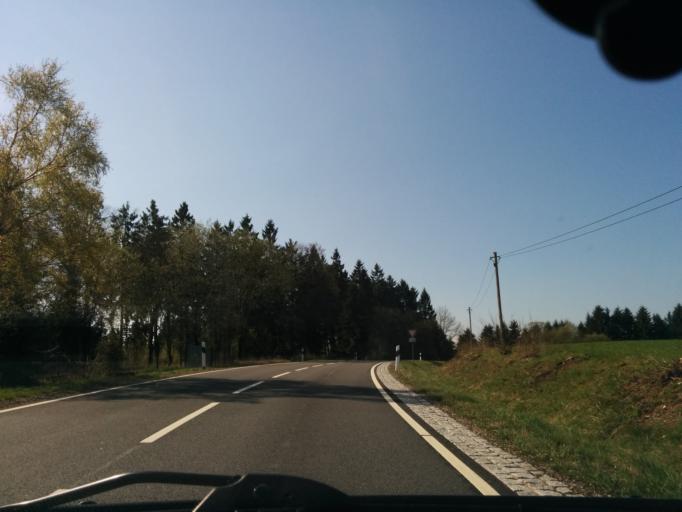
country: DE
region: Lower Saxony
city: Clausthal-Zellerfeld
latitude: 51.7965
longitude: 10.3612
